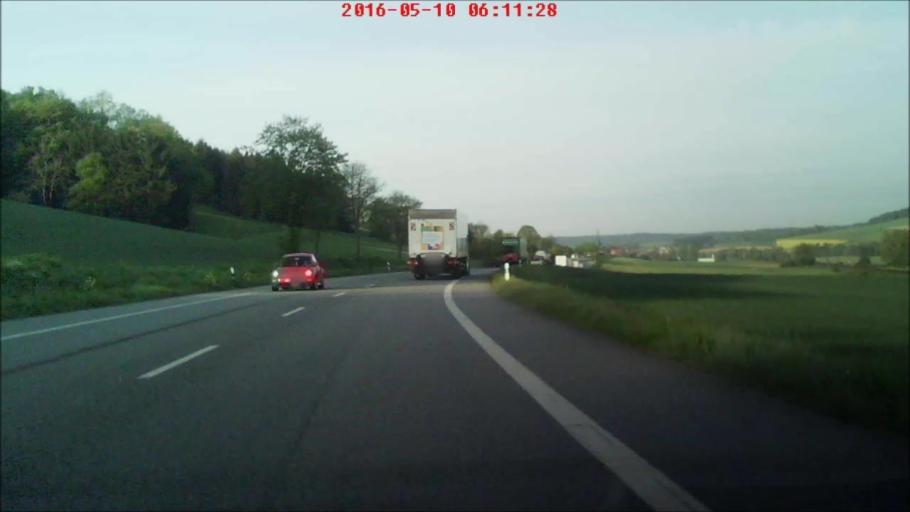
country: DE
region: Hesse
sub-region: Regierungsbezirk Kassel
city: Burghaun
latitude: 50.7836
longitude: 9.7120
